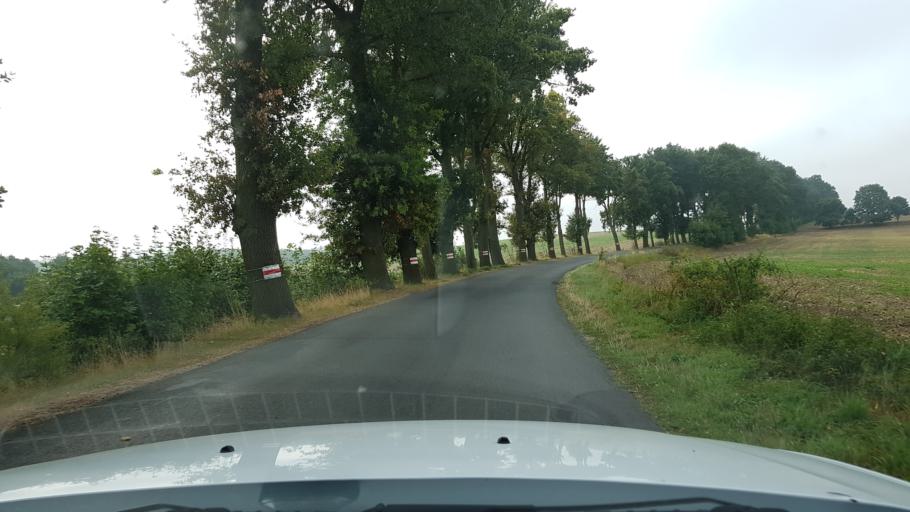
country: PL
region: West Pomeranian Voivodeship
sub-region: Powiat gryfinski
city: Moryn
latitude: 52.8950
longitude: 14.3780
